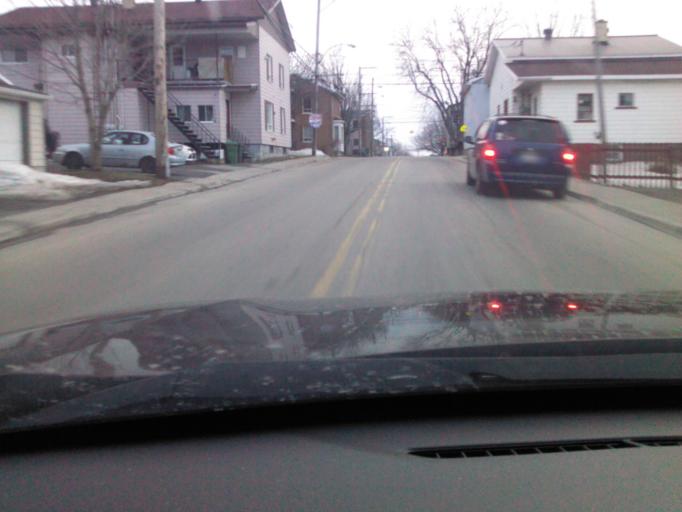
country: CA
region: Quebec
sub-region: Capitale-Nationale
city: Donnacona
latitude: 46.6756
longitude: -71.7371
